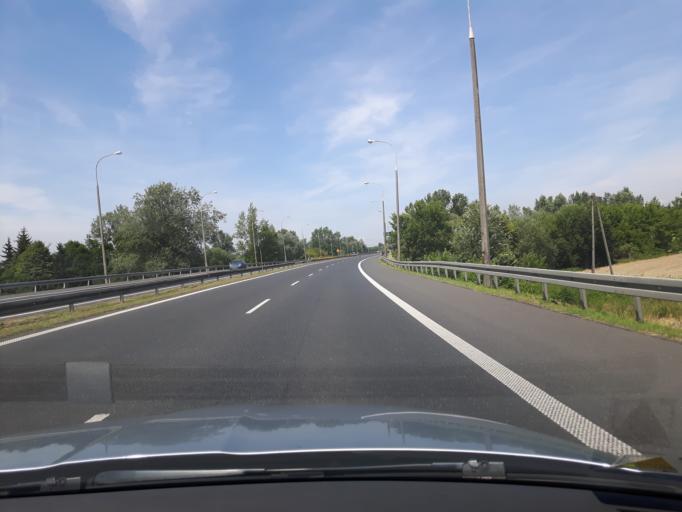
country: PL
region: Masovian Voivodeship
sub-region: Powiat nowodworski
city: Zakroczym
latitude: 52.4223
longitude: 20.6601
